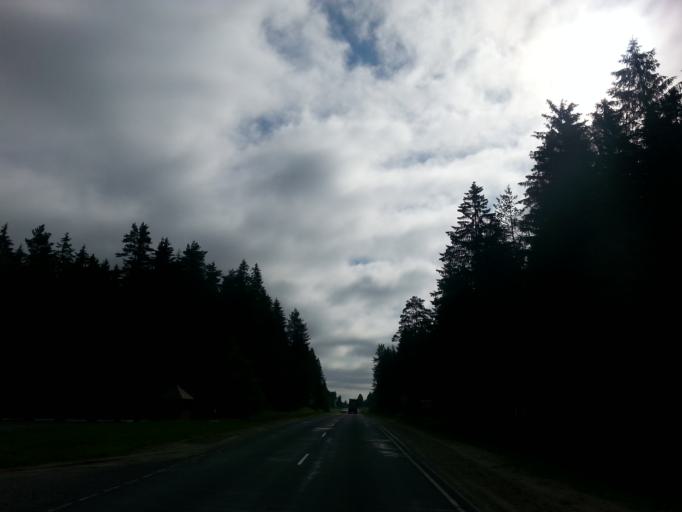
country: BY
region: Vitebsk
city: Mosar
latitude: 55.0787
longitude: 27.4384
